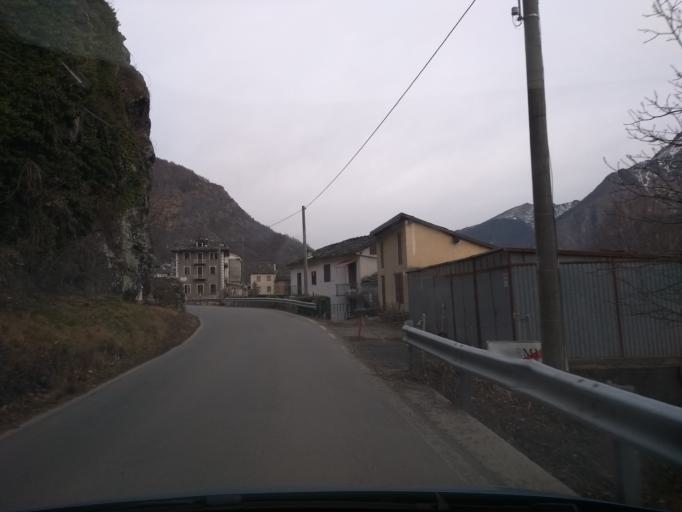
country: IT
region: Piedmont
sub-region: Provincia di Torino
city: Lemie
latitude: 45.2286
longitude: 7.2881
